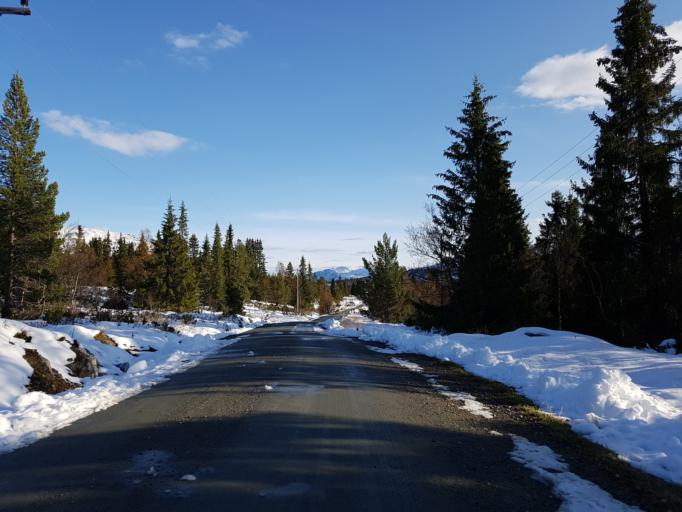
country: NO
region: Oppland
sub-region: Sel
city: Otta
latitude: 61.8156
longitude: 9.6792
